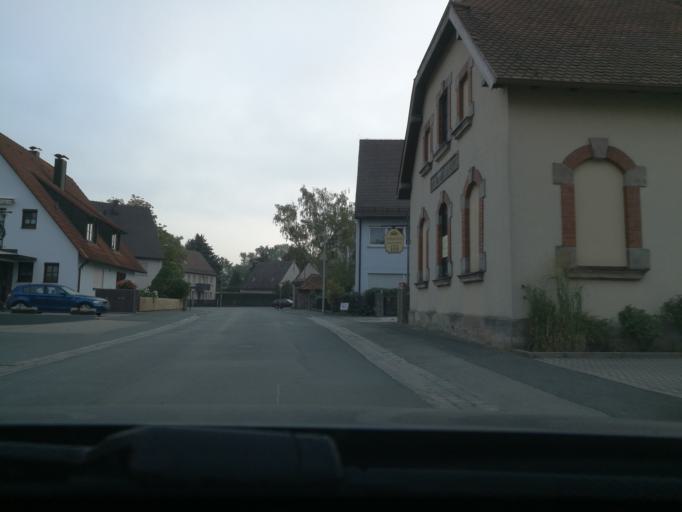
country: DE
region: Bavaria
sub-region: Regierungsbezirk Mittelfranken
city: Wetzendorf
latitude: 49.4964
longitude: 11.0446
